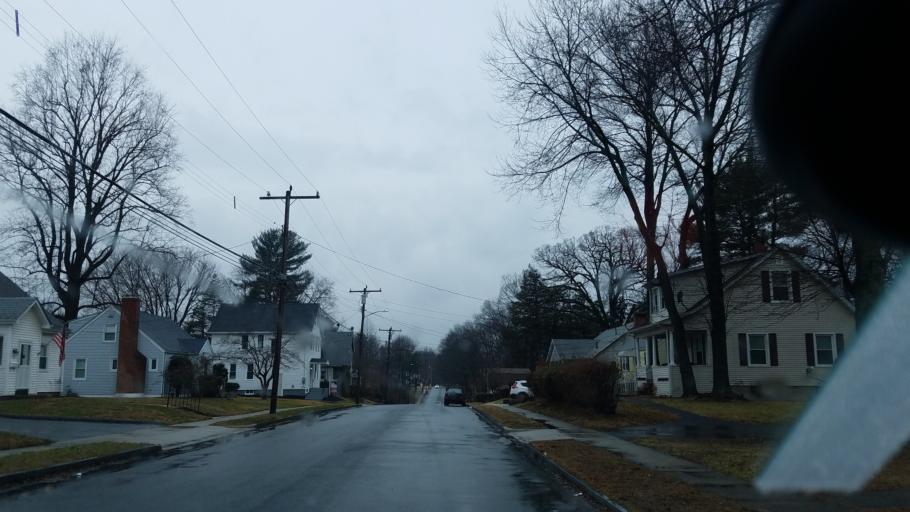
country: US
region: Connecticut
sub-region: Hartford County
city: West Hartford
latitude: 41.7483
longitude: -72.7165
